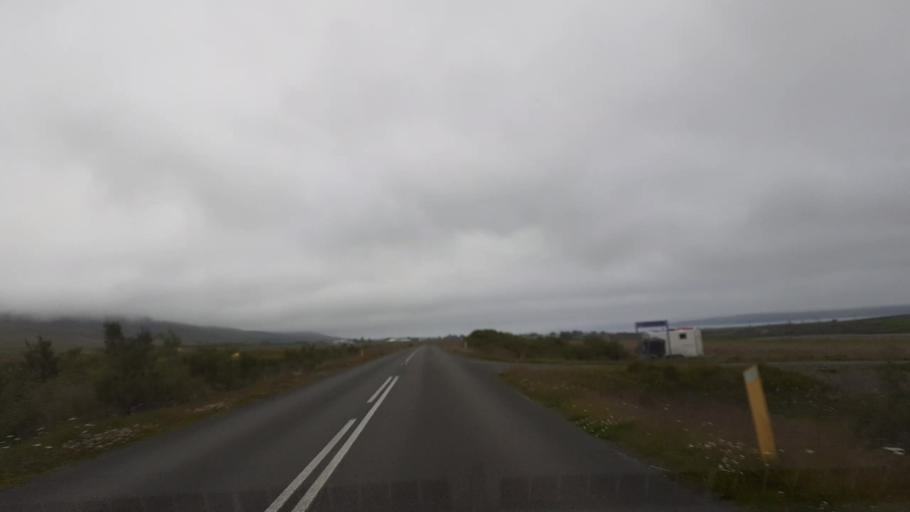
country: IS
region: Northeast
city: Dalvik
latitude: 65.9508
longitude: -18.5539
